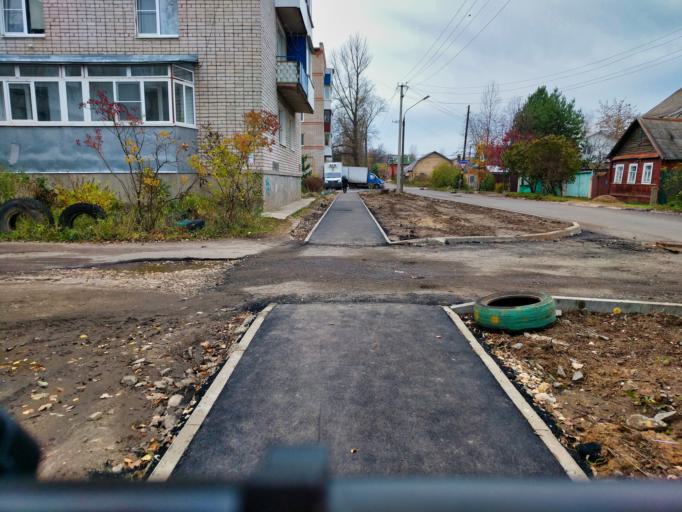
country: RU
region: Tverskaya
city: Rzhev
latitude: 56.2494
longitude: 34.3326
